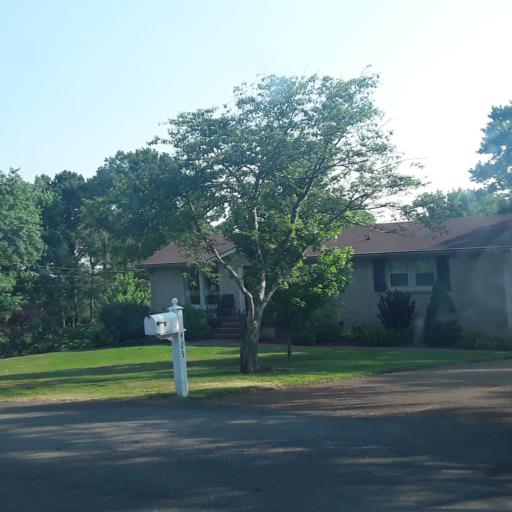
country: US
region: Tennessee
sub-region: Williamson County
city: Brentwood Estates
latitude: 36.0288
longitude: -86.7151
